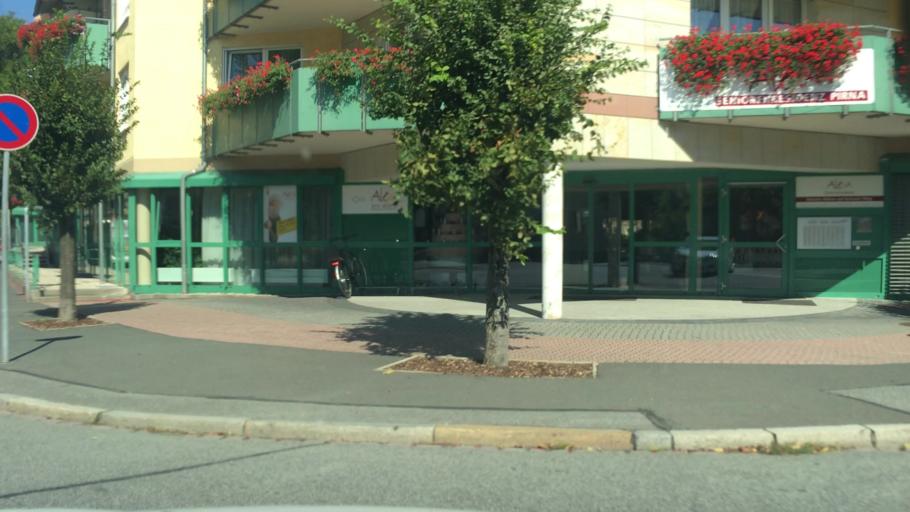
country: DE
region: Saxony
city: Pirna
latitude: 50.9597
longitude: 13.9376
